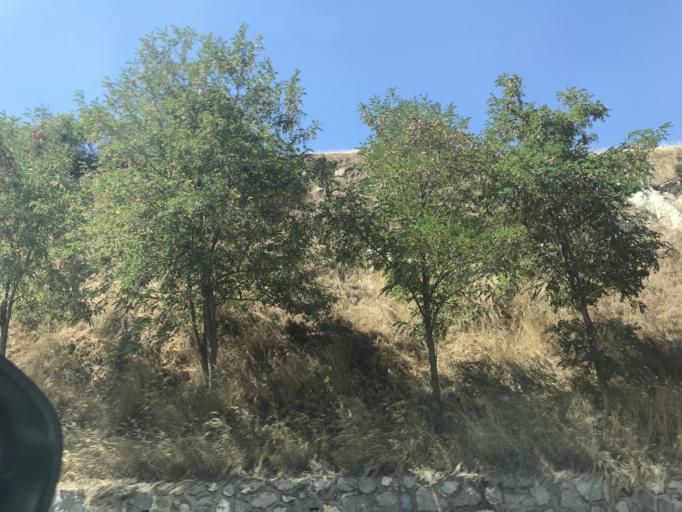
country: TR
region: Aydin
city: Cakirbeyli
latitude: 37.7325
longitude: 27.8878
